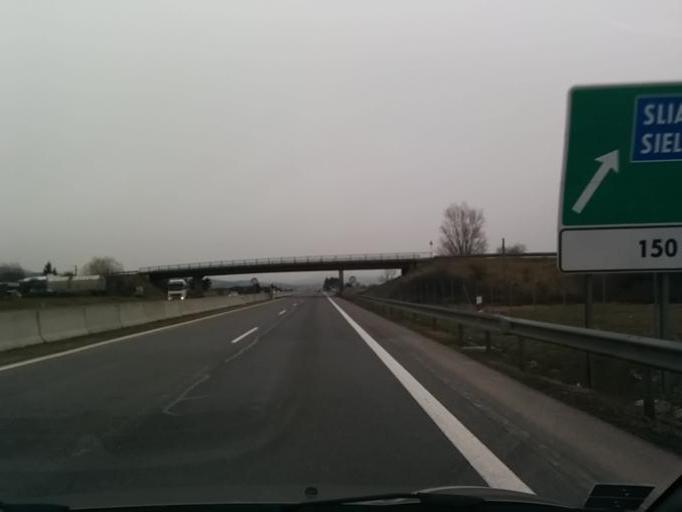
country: SK
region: Banskobystricky
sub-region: Okres Banska Bystrica
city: Zvolen
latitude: 48.6279
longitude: 19.1190
